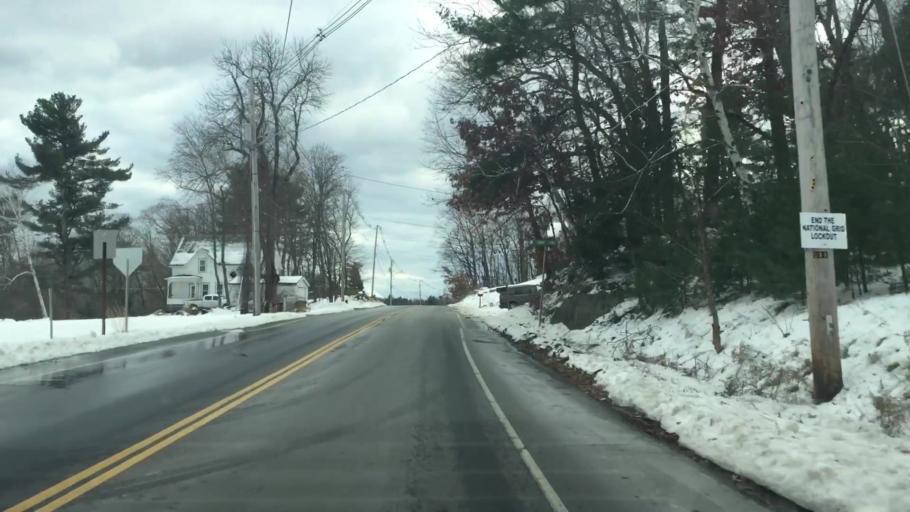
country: US
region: New Hampshire
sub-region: Hillsborough County
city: Pelham
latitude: 42.6982
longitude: -71.3518
